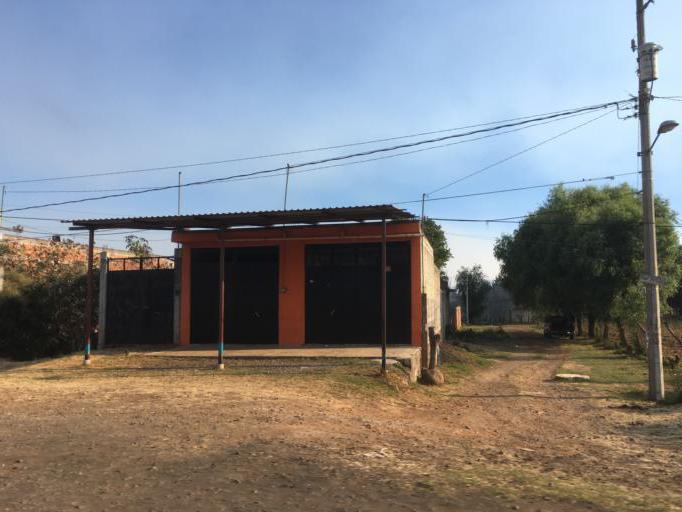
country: MX
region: Michoacan
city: Santa Fe de la Laguna
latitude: 19.6704
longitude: -101.5539
